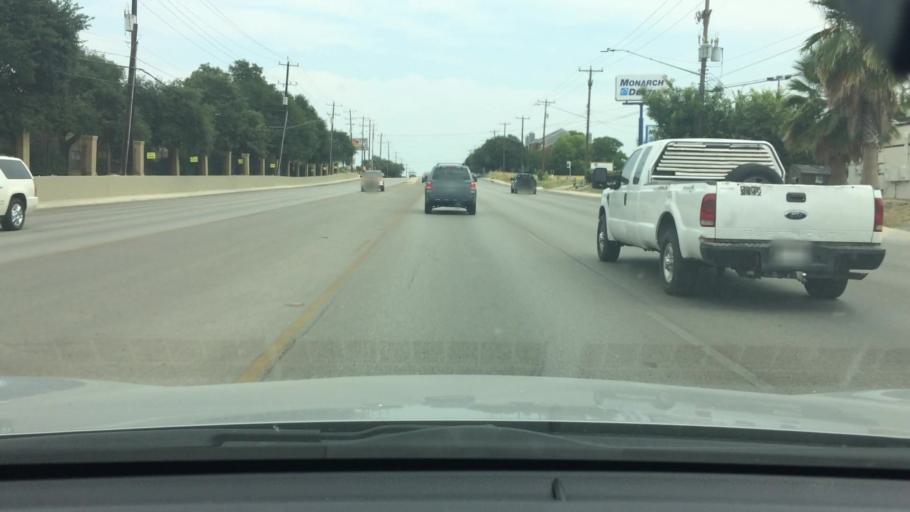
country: US
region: Texas
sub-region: Bexar County
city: Leon Valley
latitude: 29.4631
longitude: -98.6431
